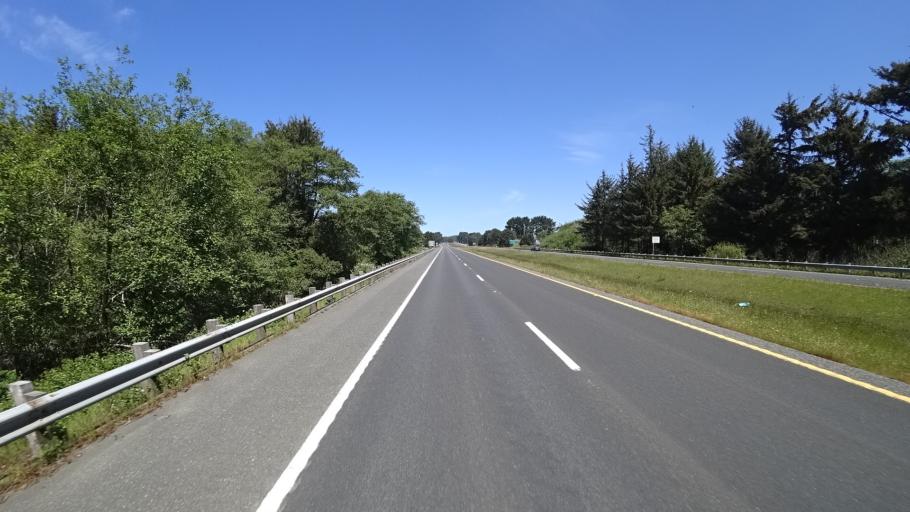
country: US
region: California
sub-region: Humboldt County
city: McKinleyville
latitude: 40.9617
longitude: -124.1163
